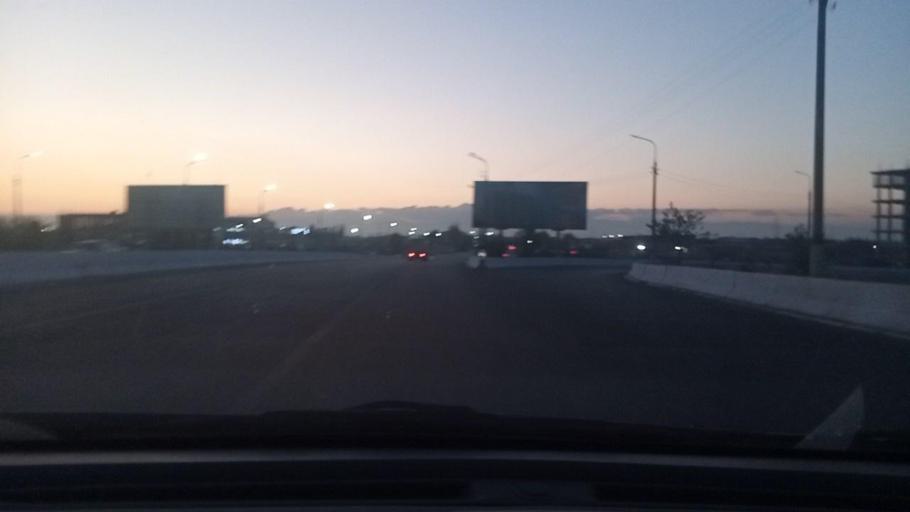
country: UZ
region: Toshkent Shahri
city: Tashkent
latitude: 41.2433
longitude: 69.2180
